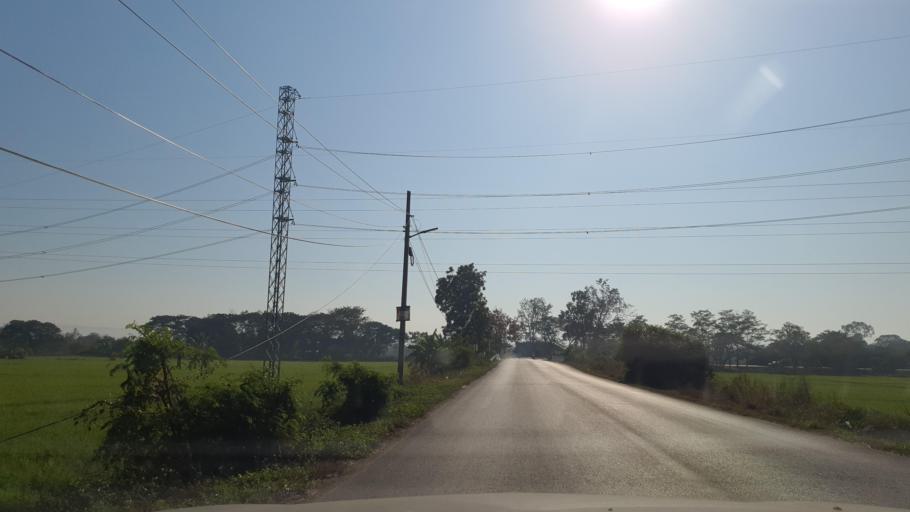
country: TH
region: Chiang Mai
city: Saraphi
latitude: 18.6762
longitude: 99.0785
